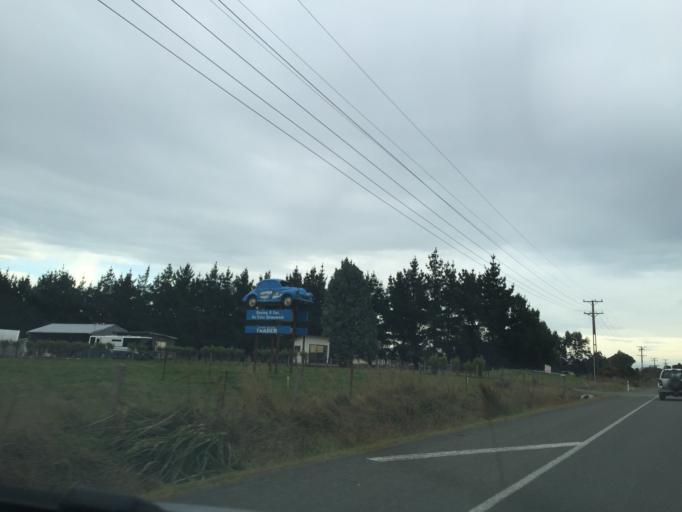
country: NZ
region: Southland
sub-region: Invercargill City
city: Invercargill
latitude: -46.4019
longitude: 168.4071
